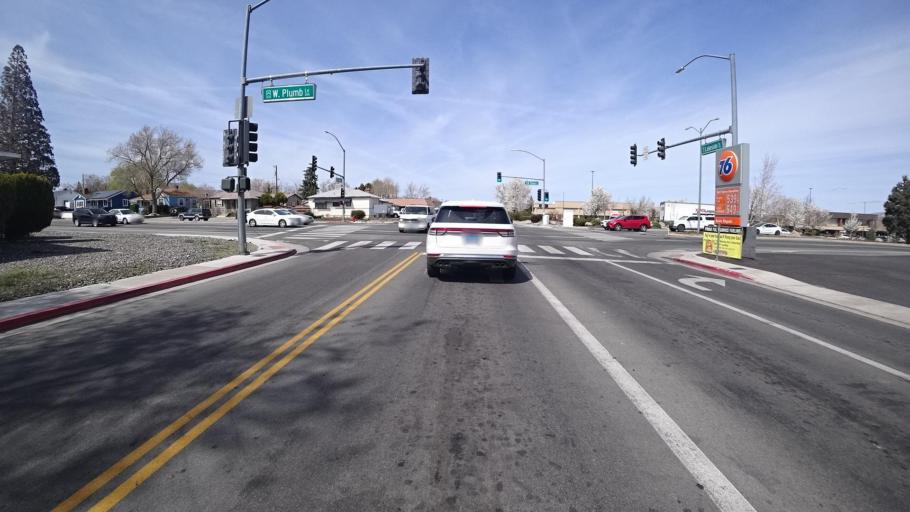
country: US
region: Nevada
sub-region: Washoe County
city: Reno
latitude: 39.5054
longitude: -119.8073
